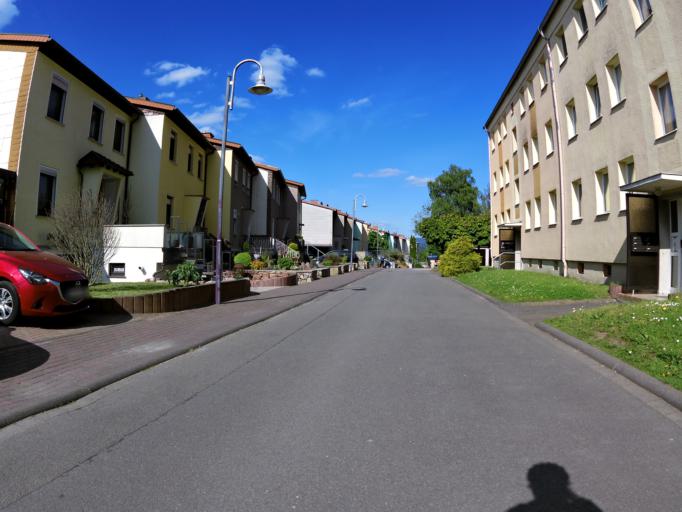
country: DE
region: Thuringia
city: Bad Salzungen
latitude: 50.8030
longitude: 10.2209
